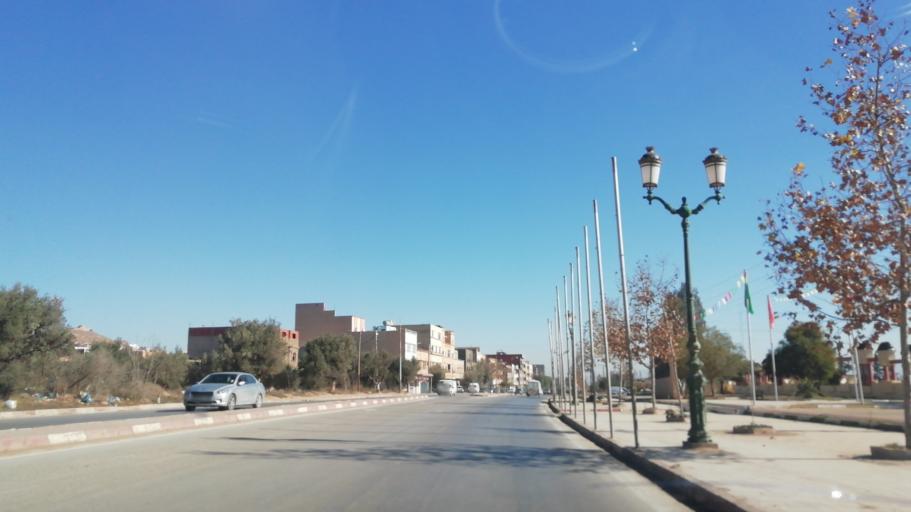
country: DZ
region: Tlemcen
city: Nedroma
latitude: 34.8442
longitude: -1.7572
